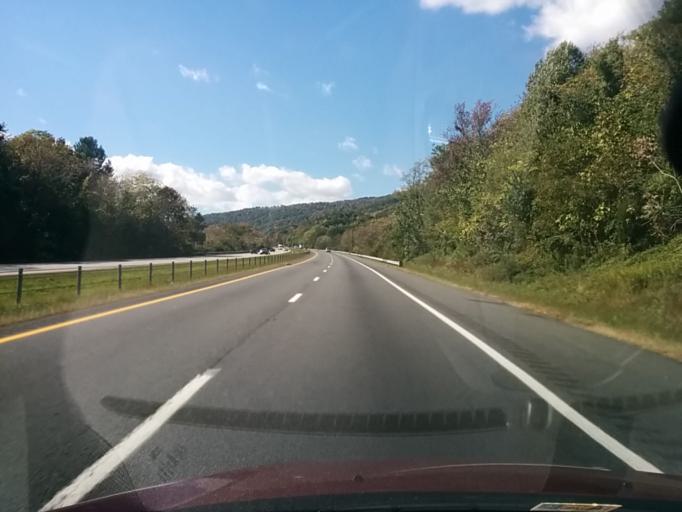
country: US
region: Virginia
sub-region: Albemarle County
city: Crozet
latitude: 38.0472
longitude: -78.7714
